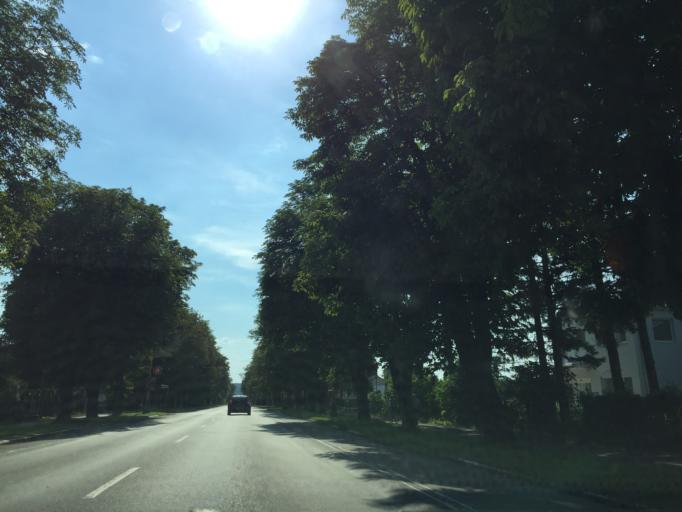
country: SK
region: Kosicky
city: Strazske
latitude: 48.8725
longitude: 21.8327
